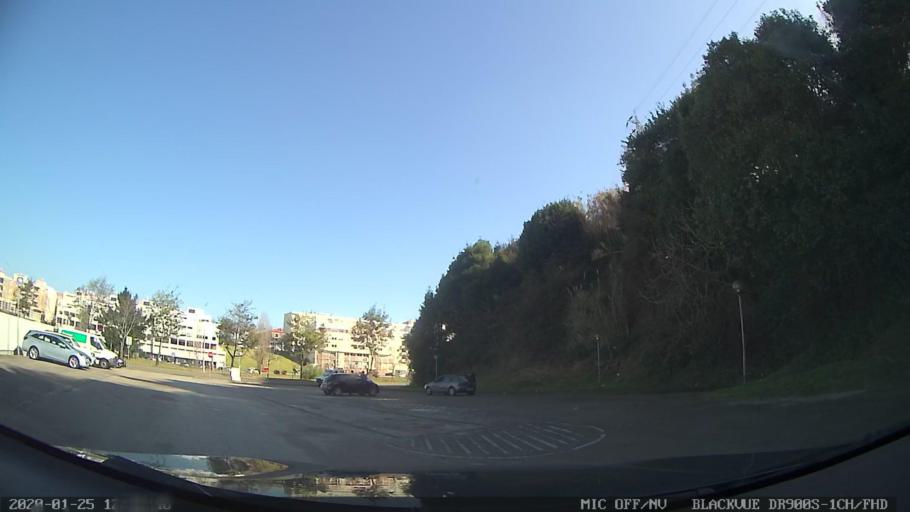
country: PT
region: Aveiro
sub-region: Aveiro
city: Aveiro
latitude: 40.6364
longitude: -8.6398
